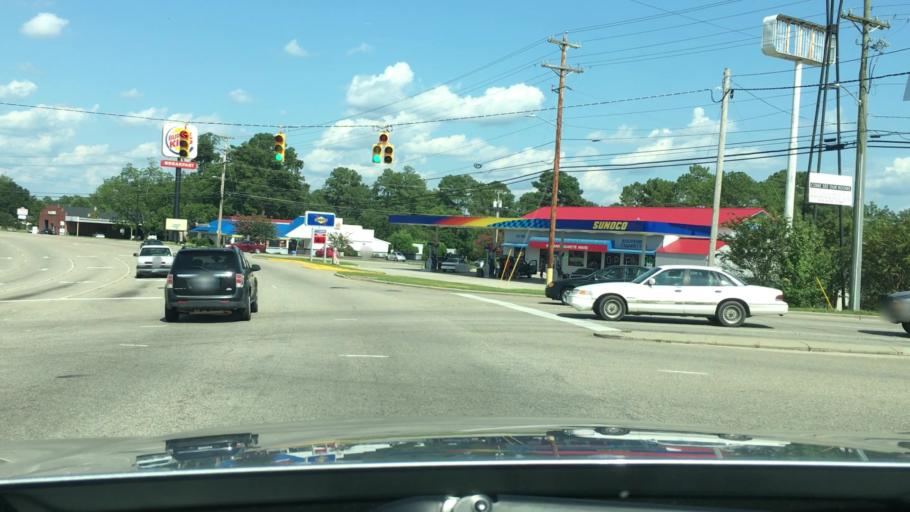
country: US
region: North Carolina
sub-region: Robeson County
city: Lumberton
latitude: 34.6221
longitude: -79.0501
